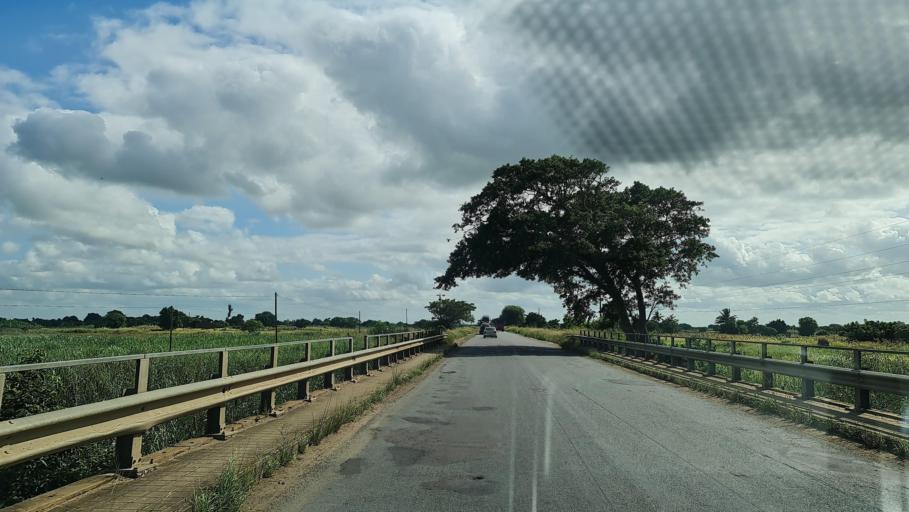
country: MZ
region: Gaza
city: Macia
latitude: -25.0860
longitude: 32.8451
